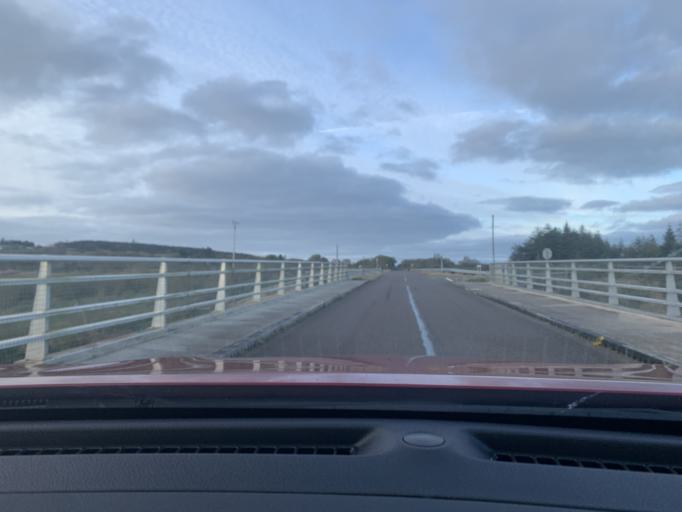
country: IE
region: Connaught
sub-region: Roscommon
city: Ballaghaderreen
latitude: 53.9218
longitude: -8.5913
